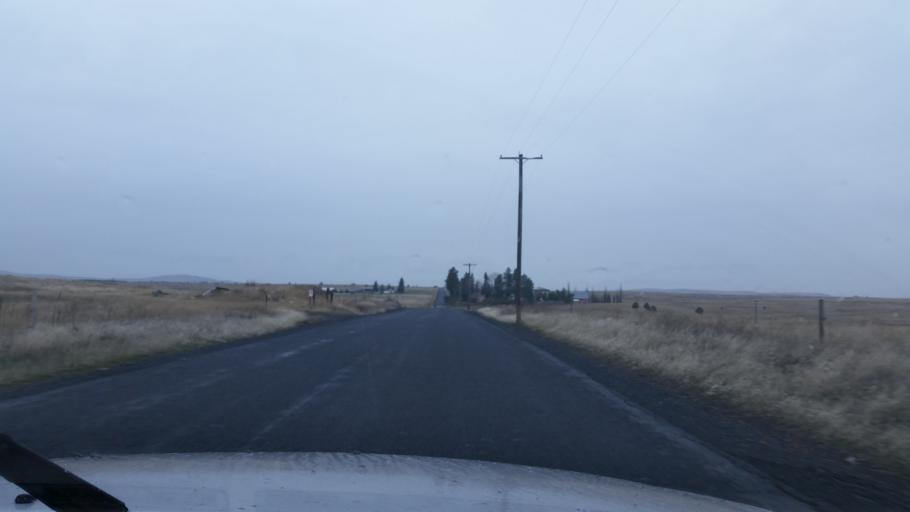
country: US
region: Washington
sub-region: Spokane County
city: Medical Lake
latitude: 47.6145
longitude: -117.7727
